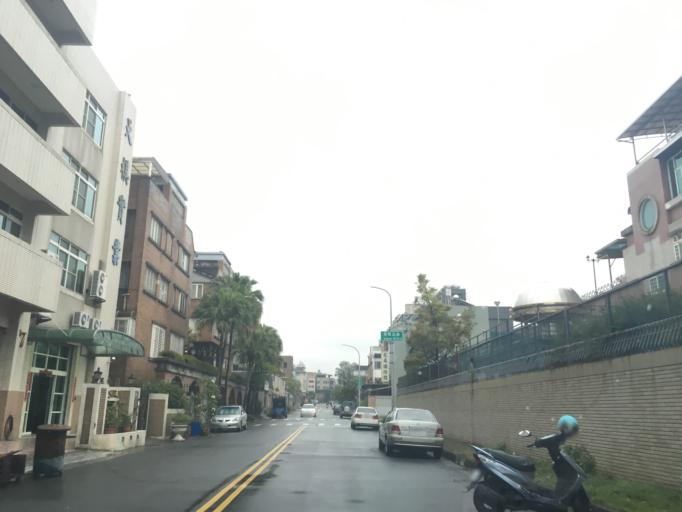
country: TW
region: Taiwan
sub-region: Taichung City
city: Taichung
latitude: 24.1710
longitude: 120.7144
